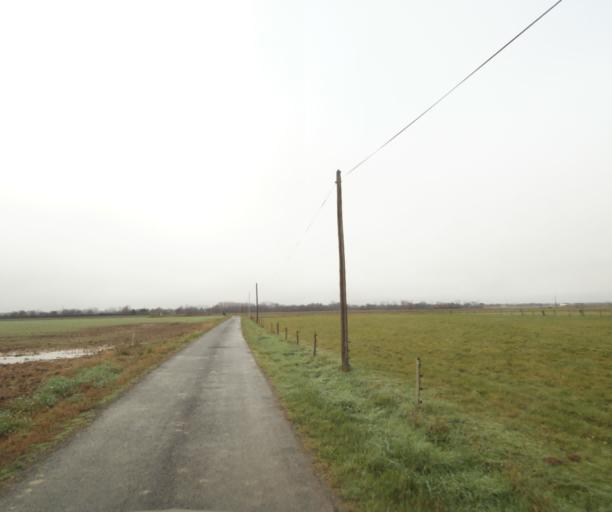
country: FR
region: Midi-Pyrenees
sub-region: Departement du Tarn-et-Garonne
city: Nohic
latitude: 43.8883
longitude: 1.4719
